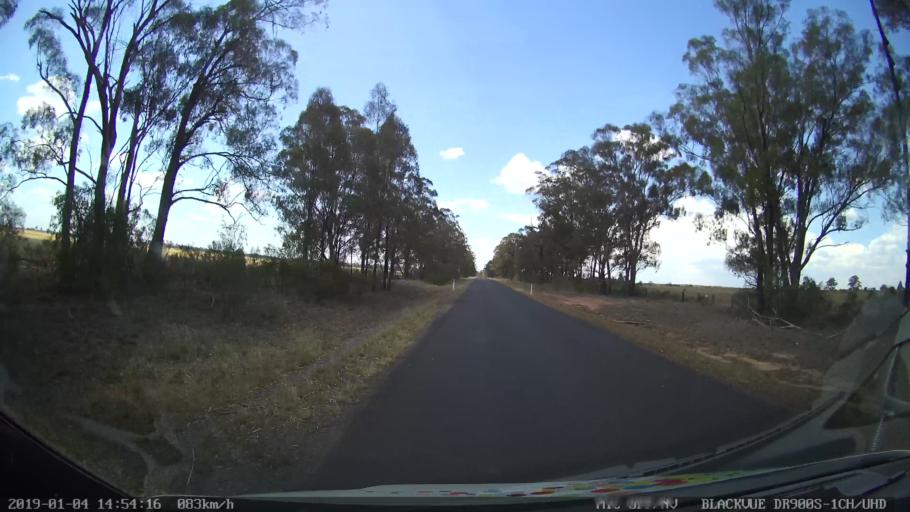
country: AU
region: New South Wales
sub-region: Dubbo Municipality
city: Dubbo
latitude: -31.9930
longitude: 148.6536
